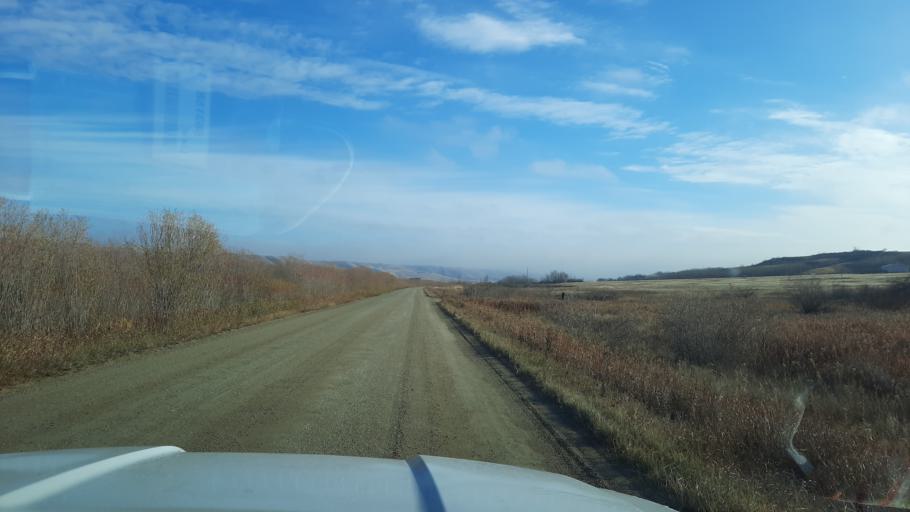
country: CA
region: Saskatchewan
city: Pilot Butte
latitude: 50.7815
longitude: -104.2686
